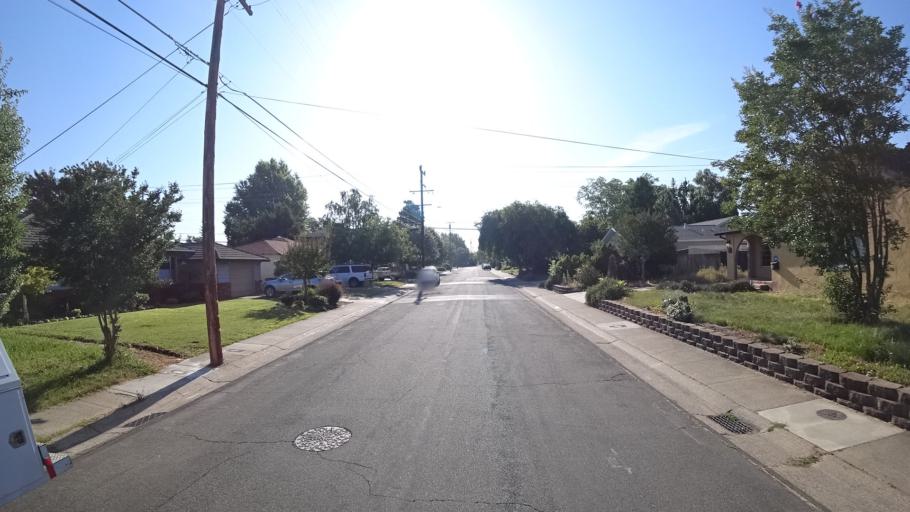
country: US
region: California
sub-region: Sacramento County
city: Florin
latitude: 38.5361
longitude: -121.4229
